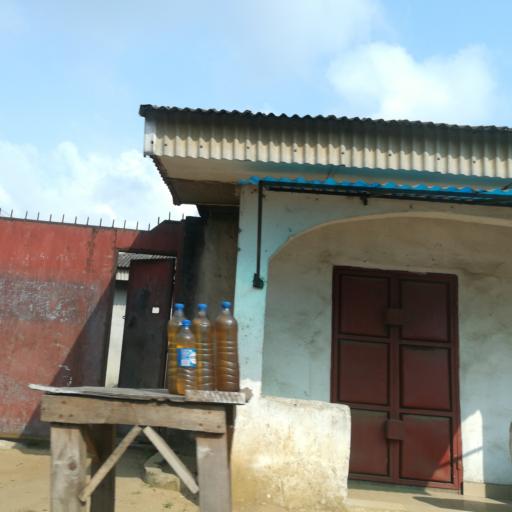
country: NG
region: Rivers
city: Okrika
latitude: 4.7781
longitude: 7.1334
